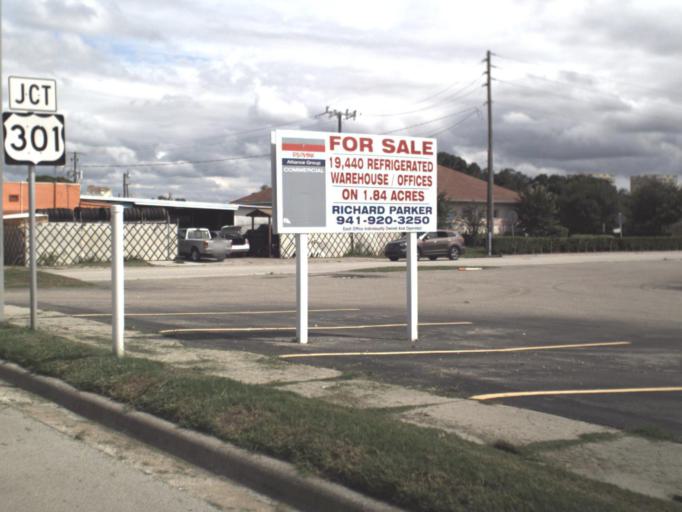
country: US
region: Florida
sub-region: Manatee County
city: Palmetto
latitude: 27.5211
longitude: -82.5665
